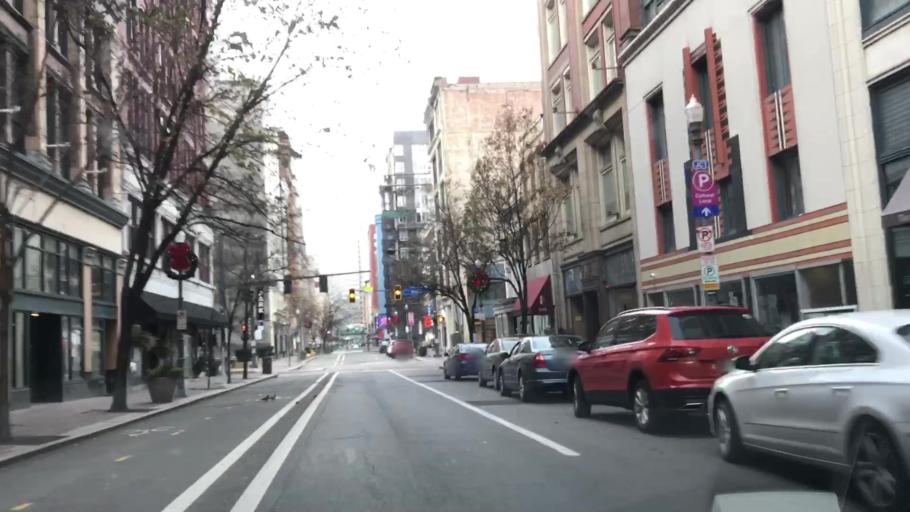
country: US
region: Pennsylvania
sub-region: Allegheny County
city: Pittsburgh
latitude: 40.4439
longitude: -79.9976
